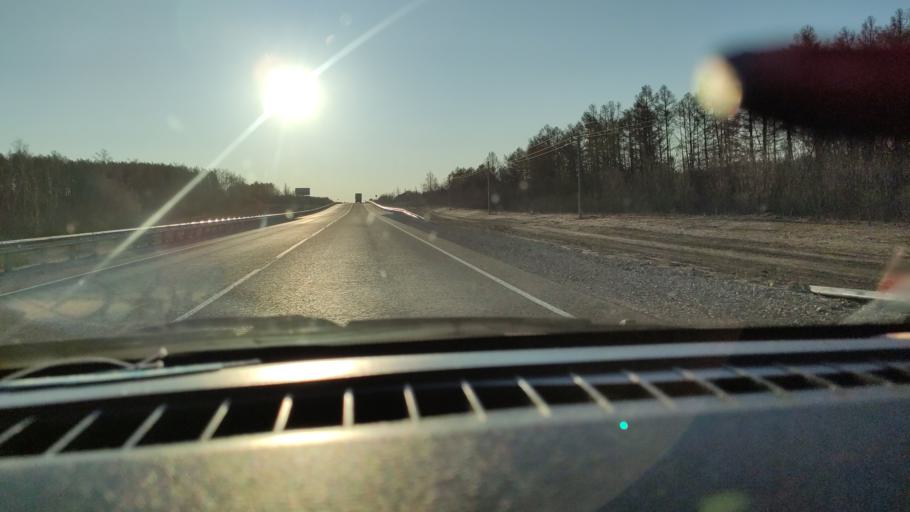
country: RU
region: Saratov
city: Shikhany
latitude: 52.1611
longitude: 47.1506
